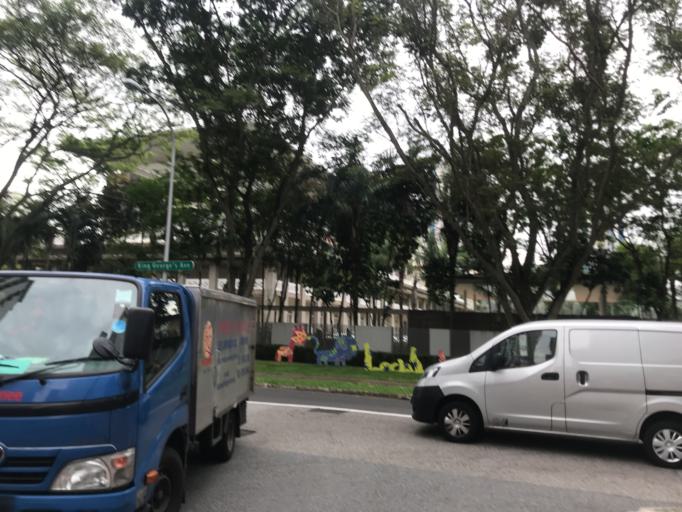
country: SG
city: Singapore
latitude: 1.3083
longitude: 103.8602
